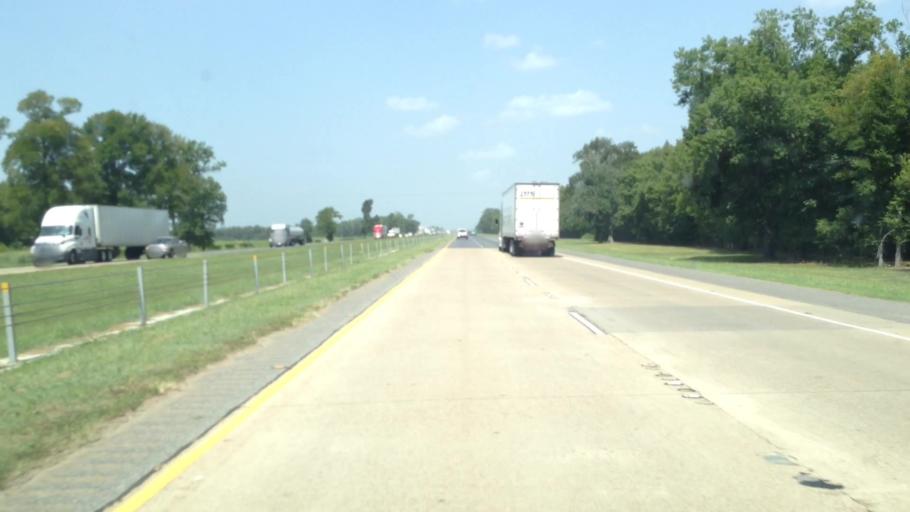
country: US
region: Louisiana
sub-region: Ouachita Parish
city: Lakeshore
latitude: 32.4900
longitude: -92.0009
